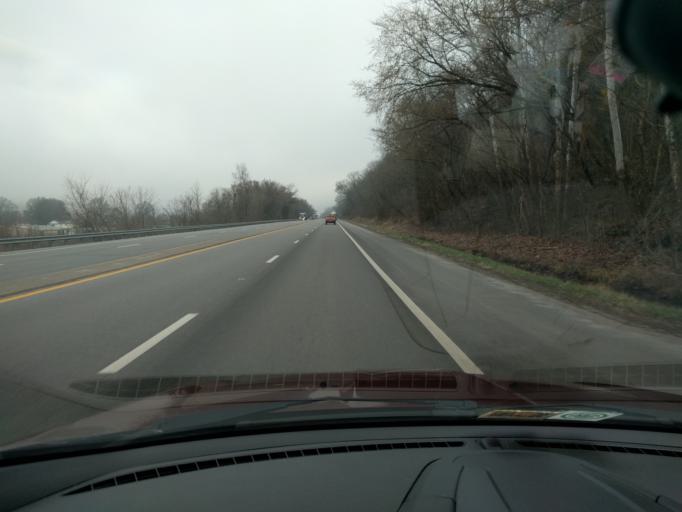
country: US
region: West Virginia
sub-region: Kanawha County
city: Marmet
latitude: 38.2609
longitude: -81.5652
